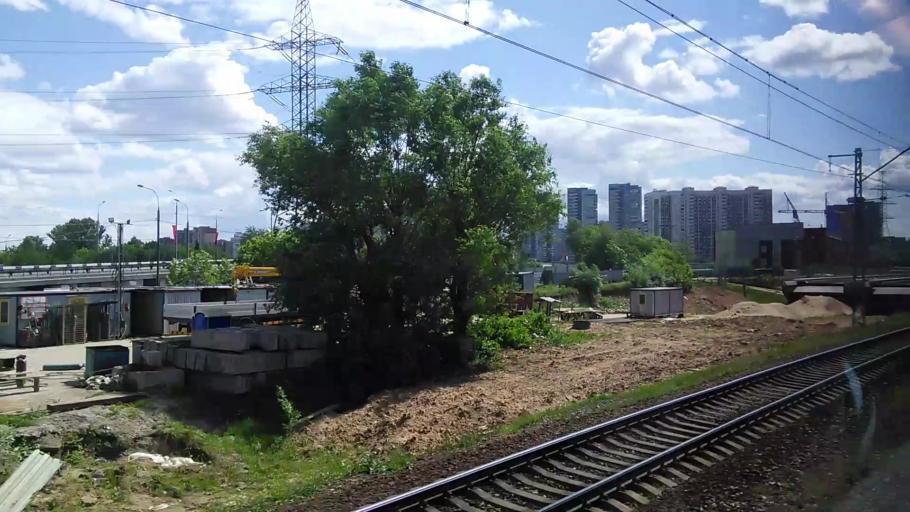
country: RU
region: Moscow
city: Novovladykino
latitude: 55.8358
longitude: 37.5773
